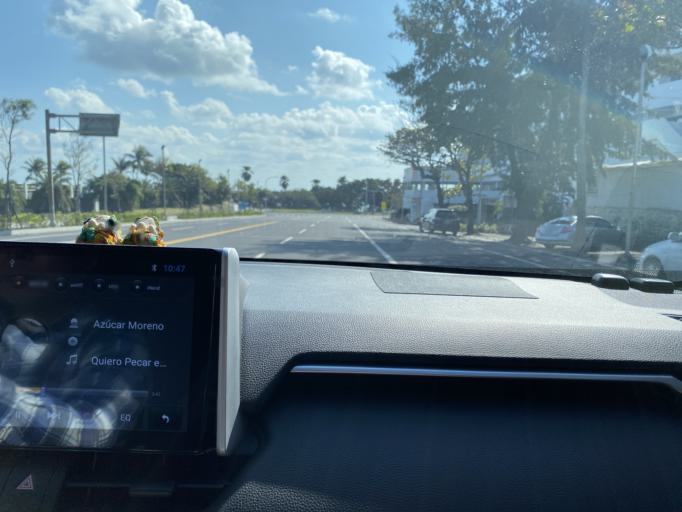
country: TW
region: Taiwan
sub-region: Hualien
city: Hualian
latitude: 23.9841
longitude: 121.6227
